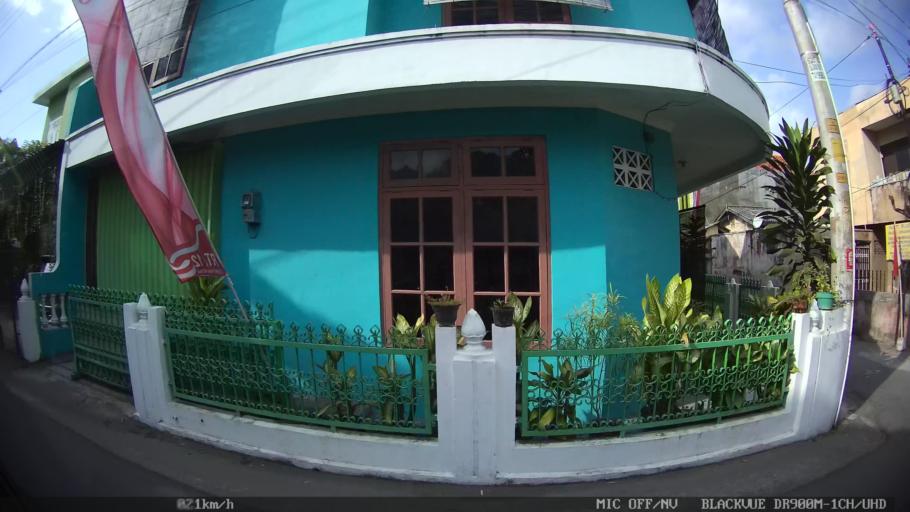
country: ID
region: Daerah Istimewa Yogyakarta
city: Kasihan
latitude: -7.8256
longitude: 110.3662
